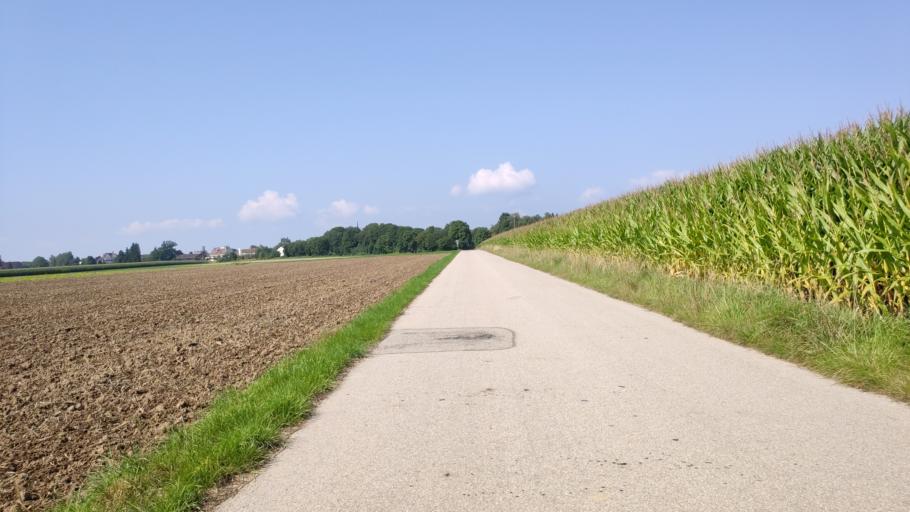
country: DE
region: Bavaria
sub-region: Swabia
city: Schwabmunchen
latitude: 48.1829
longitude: 10.7770
